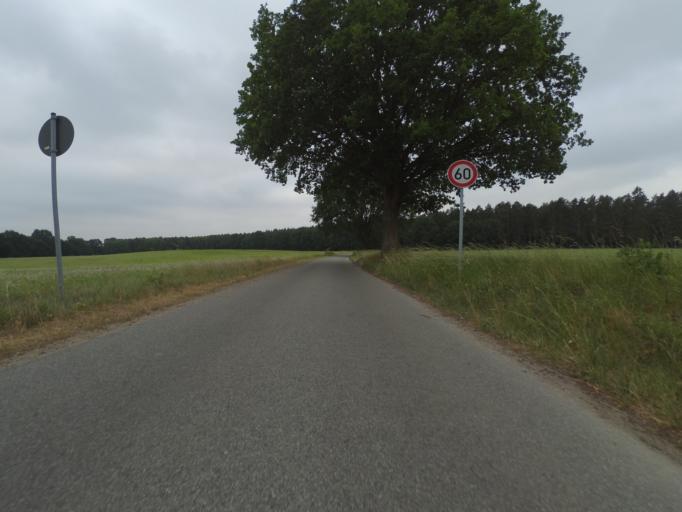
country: DE
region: Mecklenburg-Vorpommern
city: Lubz
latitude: 53.5116
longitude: 12.0801
